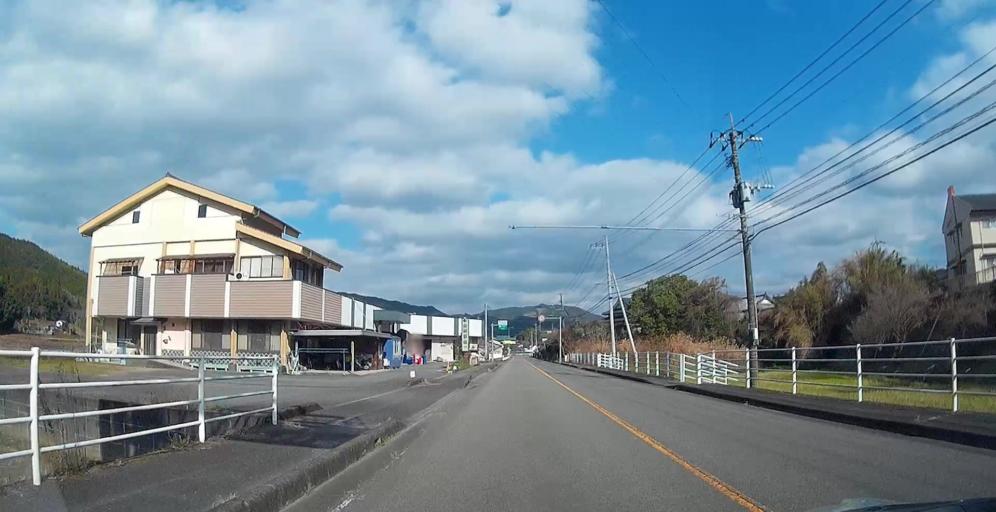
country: JP
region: Kumamoto
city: Yatsushiro
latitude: 32.3982
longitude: 130.5513
